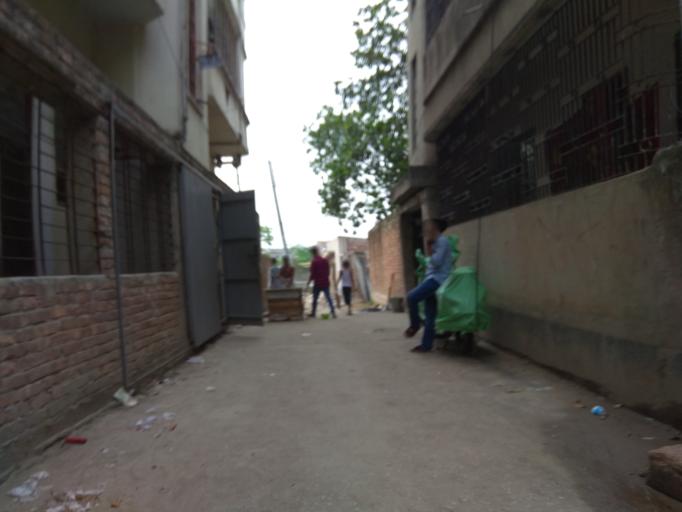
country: BD
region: Dhaka
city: Azimpur
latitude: 23.8118
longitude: 90.3800
